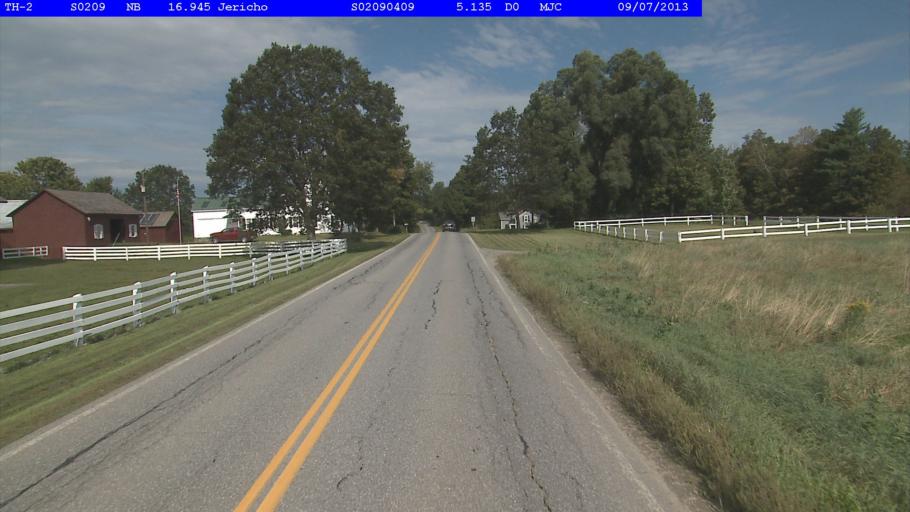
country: US
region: Vermont
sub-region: Chittenden County
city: Jericho
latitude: 44.4951
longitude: -72.9874
